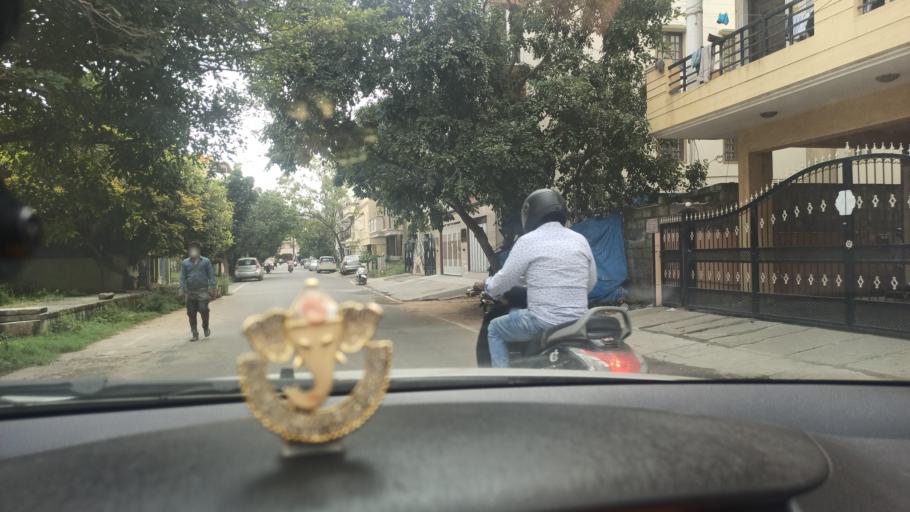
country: IN
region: Karnataka
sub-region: Bangalore Urban
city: Bangalore
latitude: 12.9114
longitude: 77.6306
